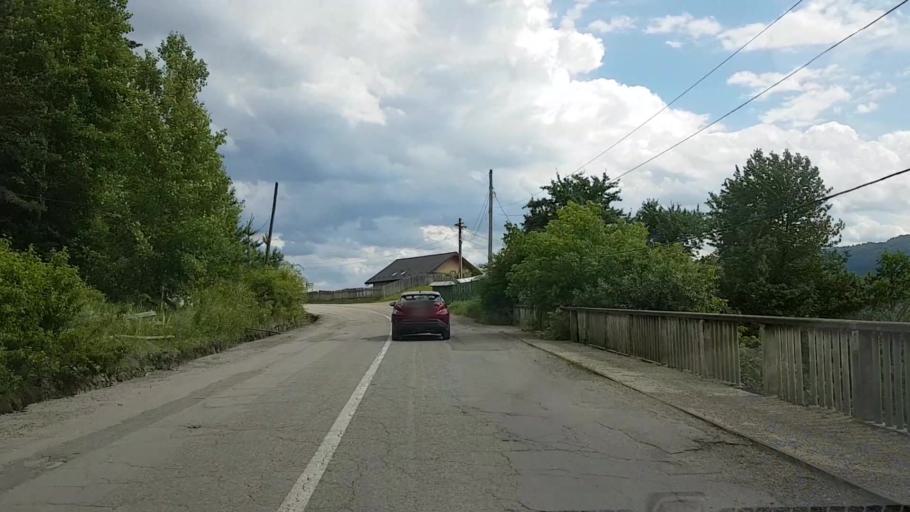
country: RO
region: Neamt
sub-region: Comuna Hangu
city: Hangu
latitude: 47.0481
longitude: 26.0396
